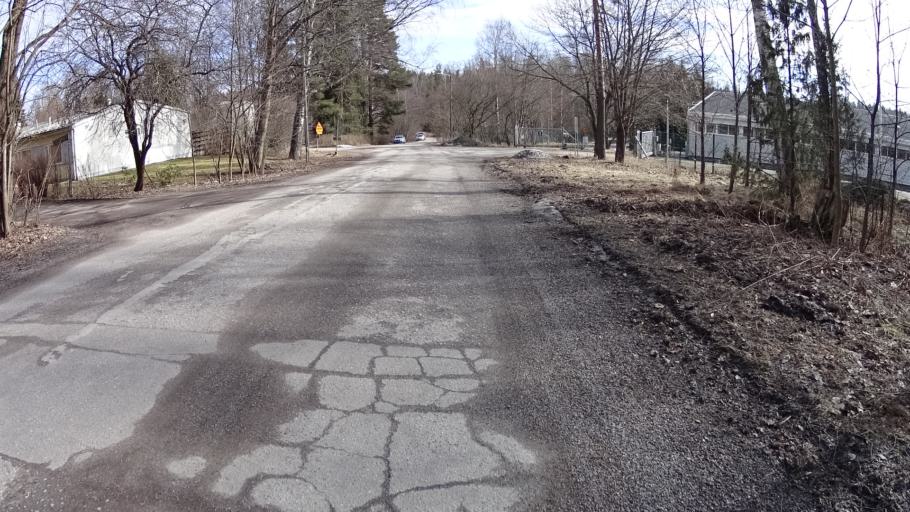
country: FI
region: Uusimaa
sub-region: Helsinki
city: Teekkarikylae
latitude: 60.2657
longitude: 24.8958
